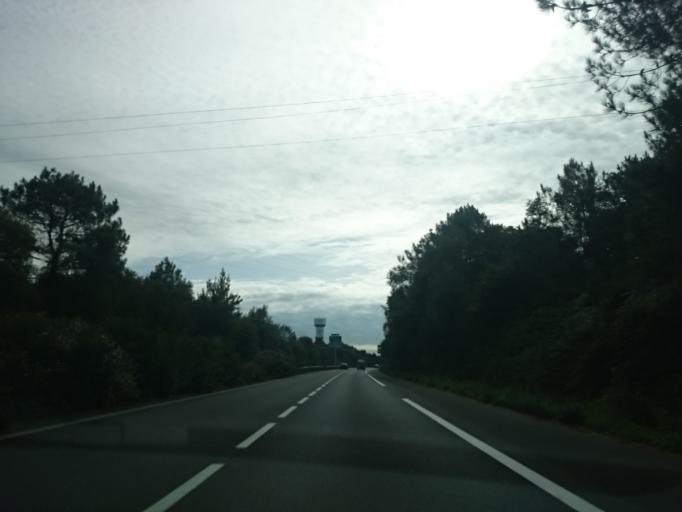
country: FR
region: Pays de la Loire
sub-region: Departement de la Loire-Atlantique
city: Missillac
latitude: 47.4806
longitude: -2.1875
